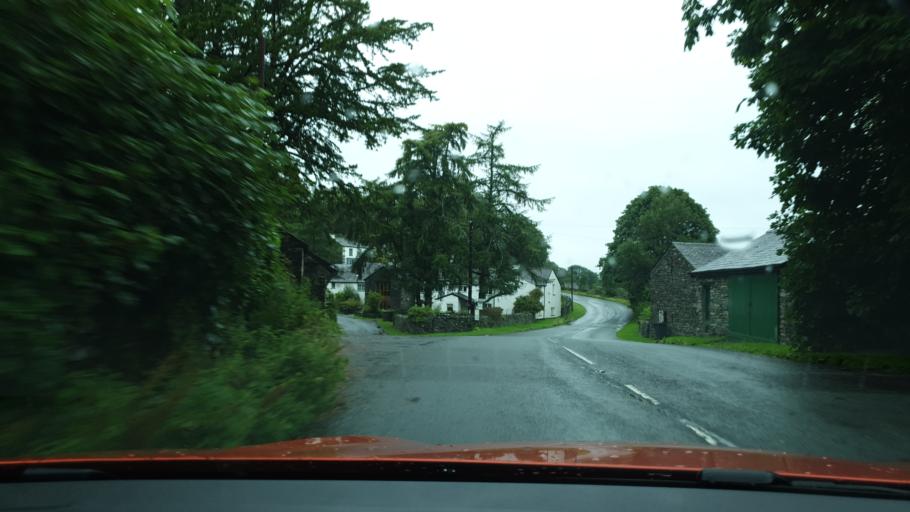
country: GB
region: England
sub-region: Cumbria
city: Ulverston
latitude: 54.2920
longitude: -3.0940
